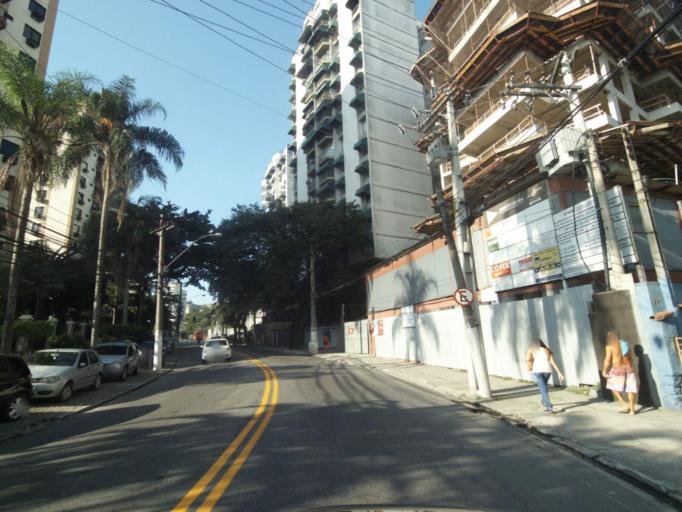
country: BR
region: Rio de Janeiro
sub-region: Niteroi
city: Niteroi
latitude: -22.8959
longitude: -43.1001
